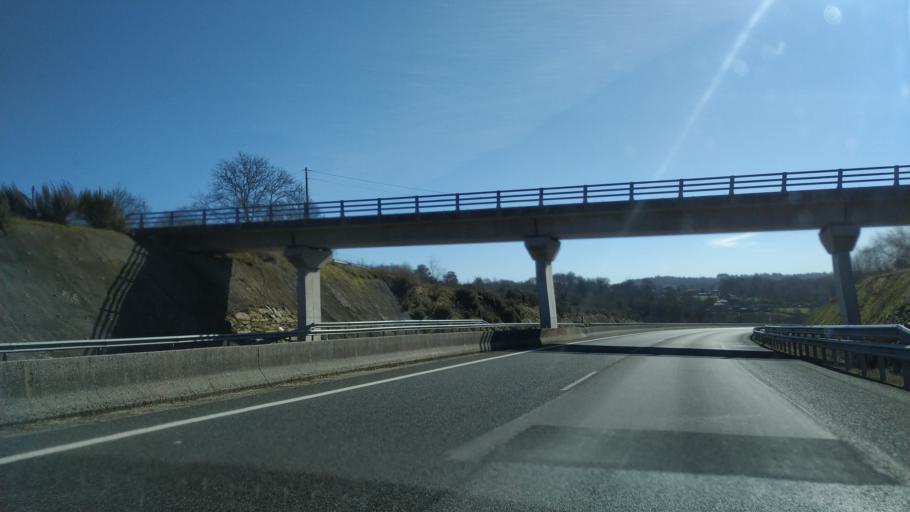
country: ES
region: Galicia
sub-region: Provincia de Pontevedra
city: Lalin
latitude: 42.6490
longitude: -8.1352
